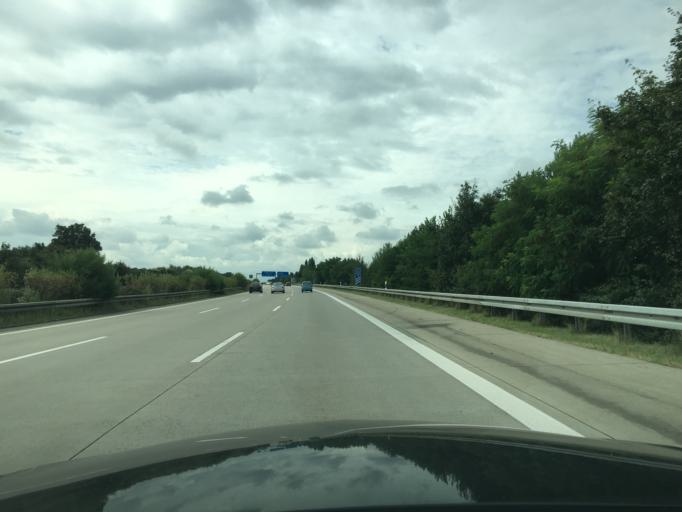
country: DE
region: Brandenburg
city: Linthe
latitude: 52.1621
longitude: 12.7861
